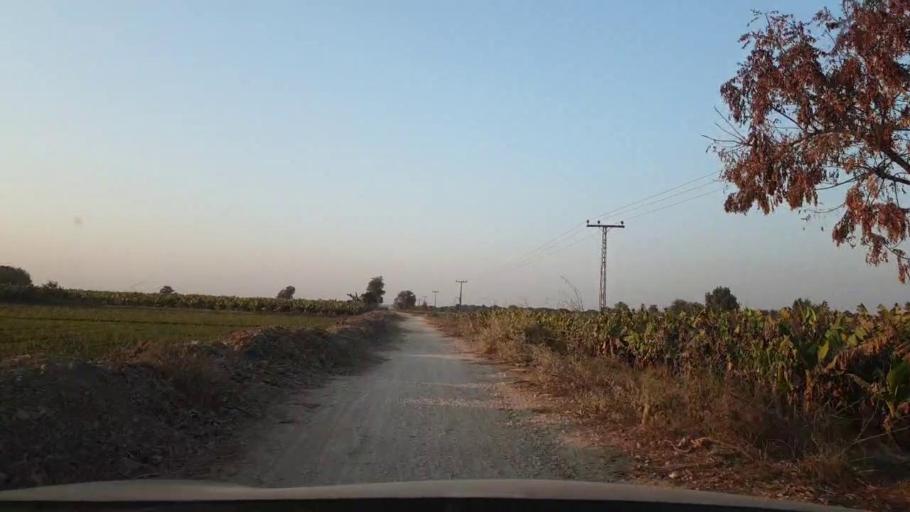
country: PK
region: Sindh
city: Tando Allahyar
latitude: 25.5139
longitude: 68.7394
